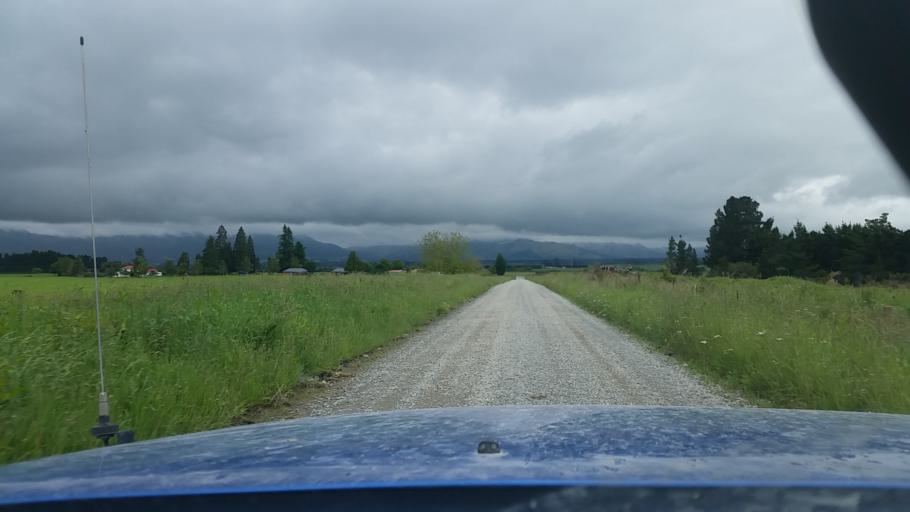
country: NZ
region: Canterbury
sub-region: Ashburton District
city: Methven
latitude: -43.7009
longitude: 171.4608
